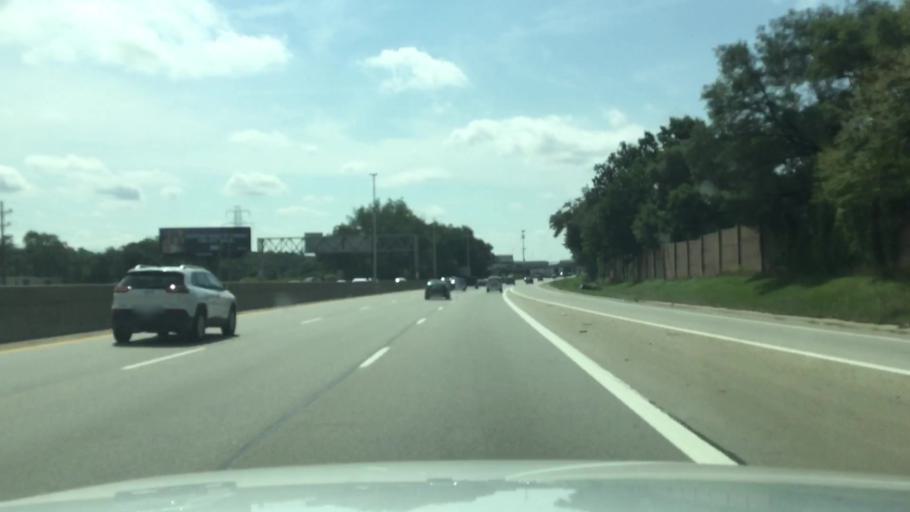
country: US
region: Michigan
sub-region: Kent County
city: Wyoming
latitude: 42.9111
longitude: -85.6772
